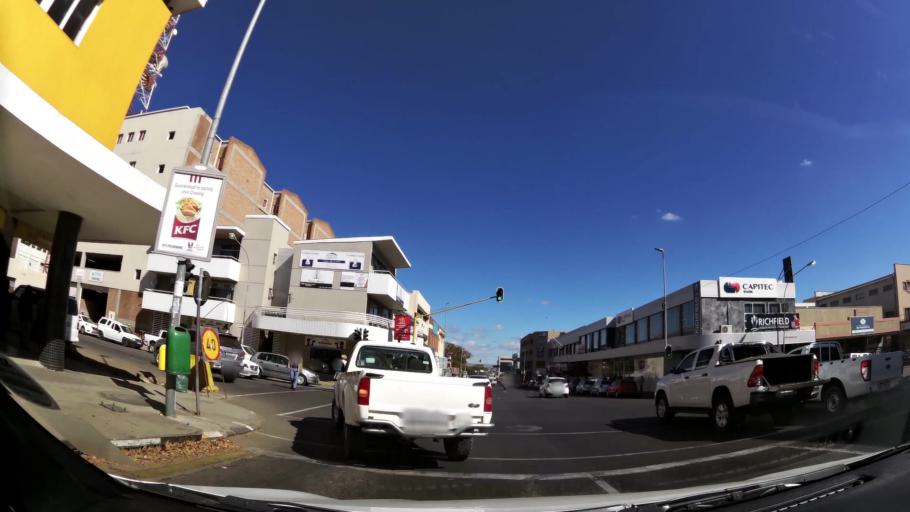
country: ZA
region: Limpopo
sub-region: Capricorn District Municipality
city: Polokwane
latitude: -23.9112
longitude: 29.4542
